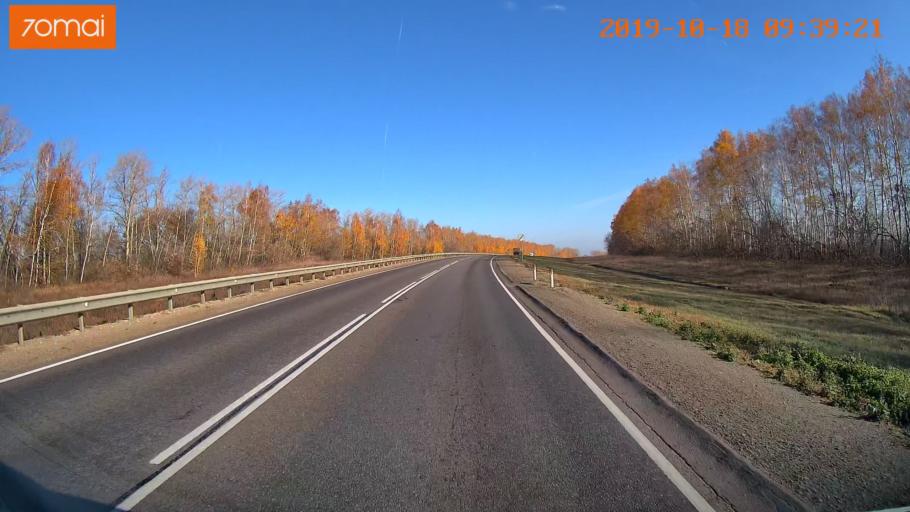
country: RU
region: Tula
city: Yefremov
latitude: 53.2521
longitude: 38.1348
